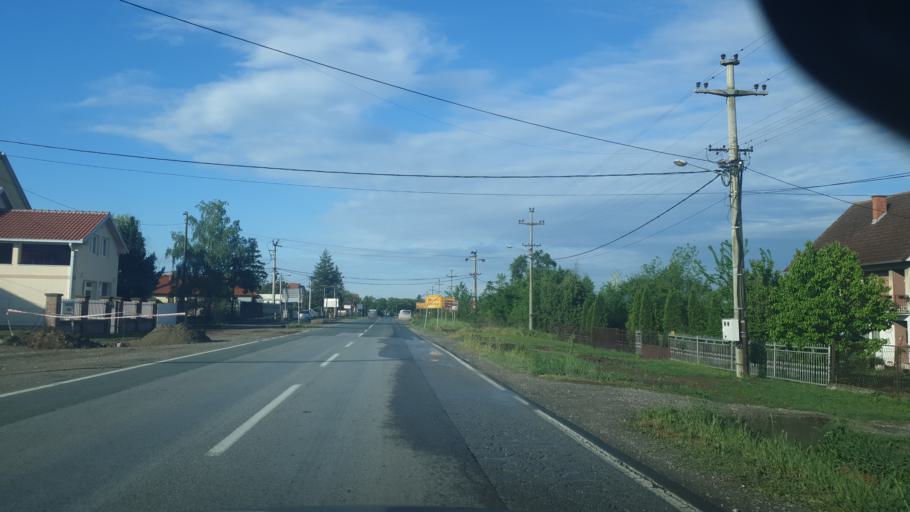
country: RS
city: Zvecka
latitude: 44.6202
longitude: 20.1709
